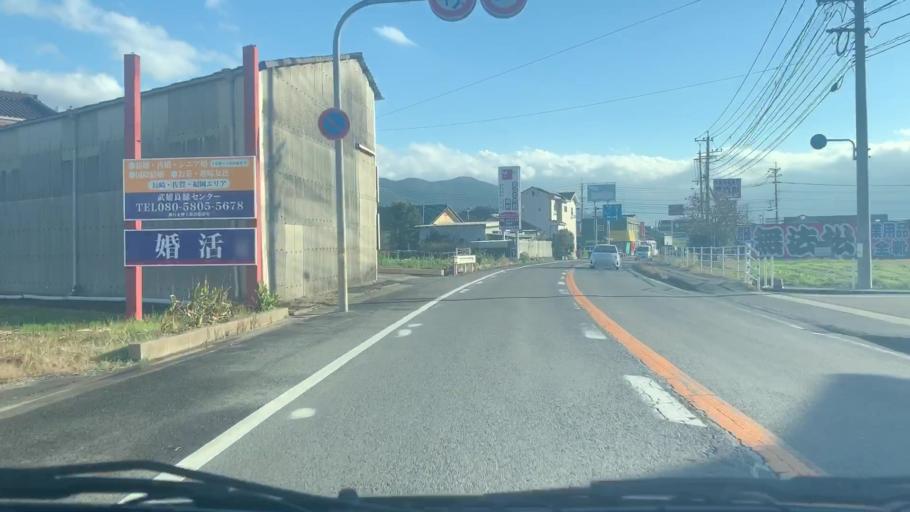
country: JP
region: Saga Prefecture
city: Takeocho-takeo
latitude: 33.2203
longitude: 130.0544
